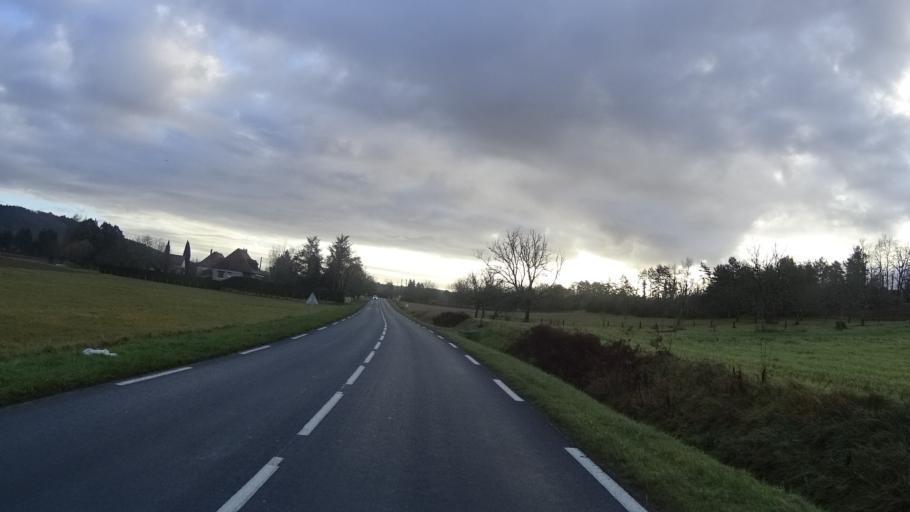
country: FR
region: Aquitaine
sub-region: Departement de la Dordogne
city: Bassillac
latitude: 45.1919
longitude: 0.8329
